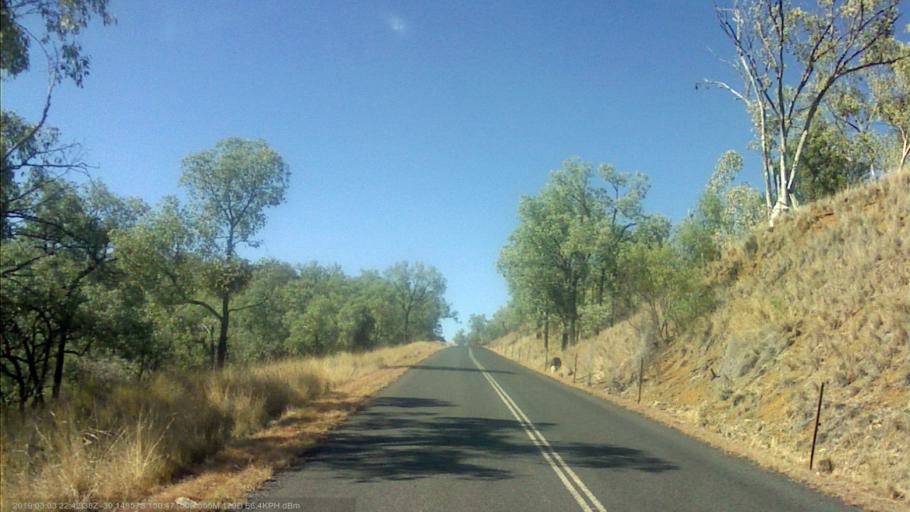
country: AU
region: New South Wales
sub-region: Gwydir
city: Bingara
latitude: -30.1496
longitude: 150.4710
